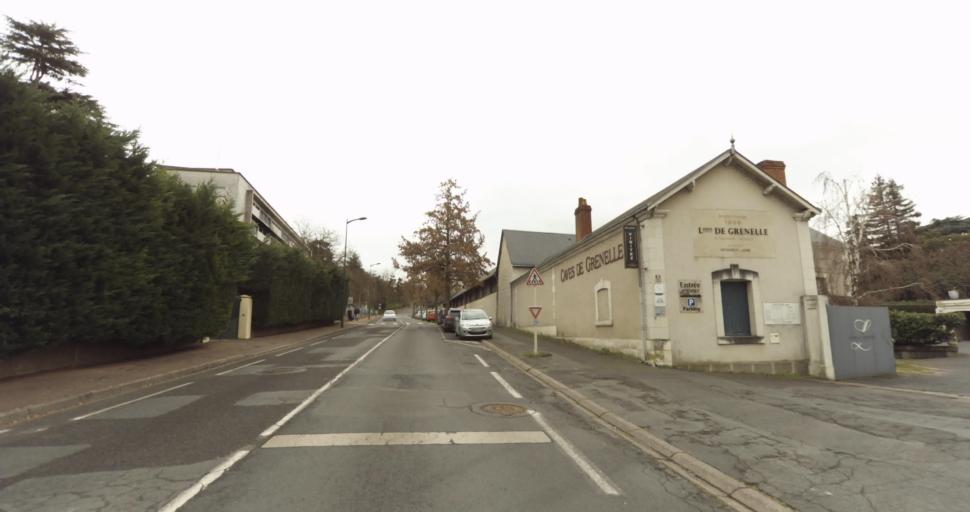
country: FR
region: Pays de la Loire
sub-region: Departement de Maine-et-Loire
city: Saumur
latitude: 47.2511
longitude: -0.0760
